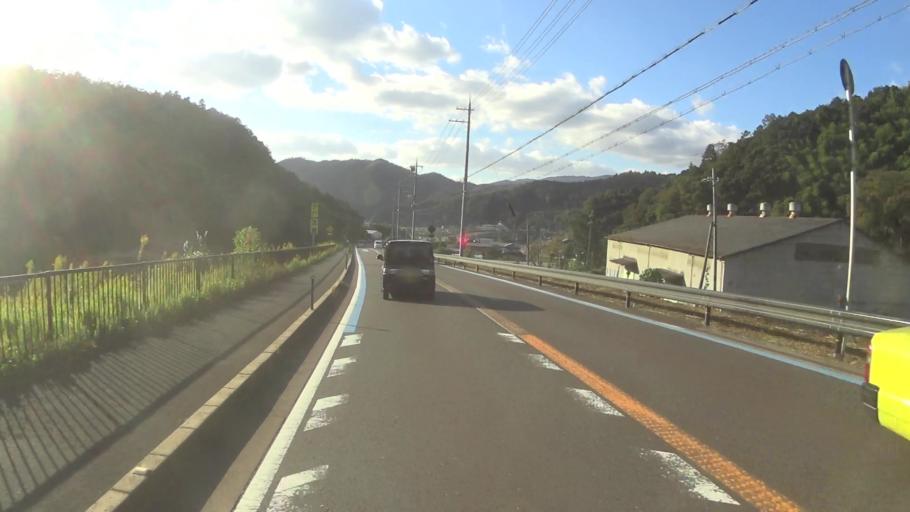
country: JP
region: Kyoto
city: Maizuru
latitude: 35.4494
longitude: 135.2741
